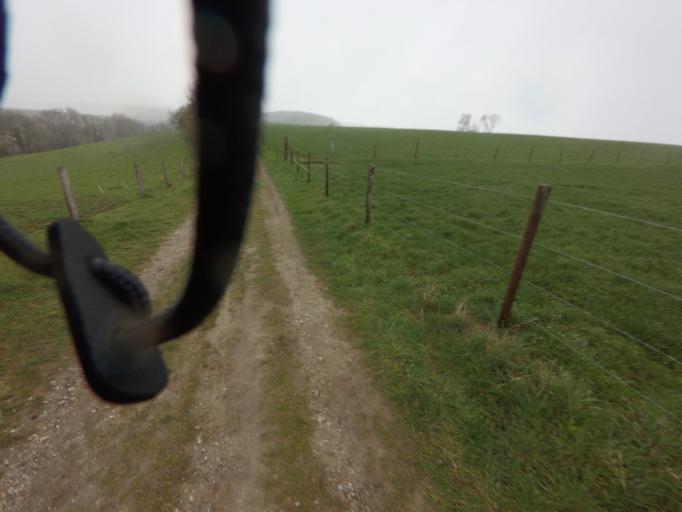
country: NL
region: Limburg
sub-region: Valkenburg aan de Geul
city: Schin op Geul
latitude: 50.8399
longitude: 5.8673
